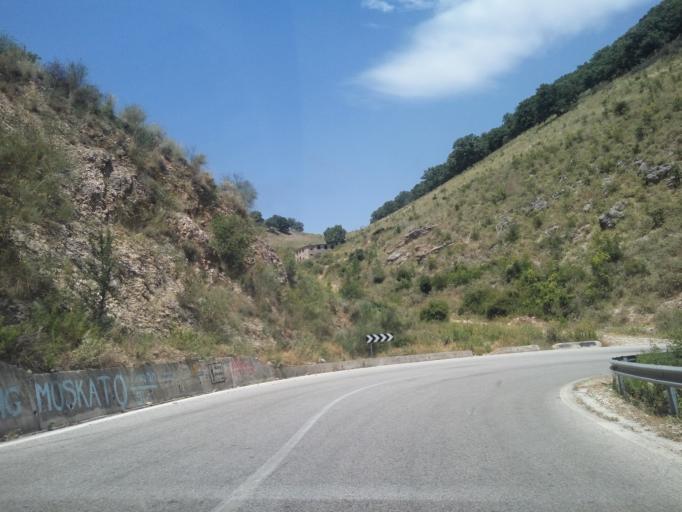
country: AL
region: Vlore
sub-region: Rrethi i Vlores
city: Himare
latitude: 40.0779
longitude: 19.7766
